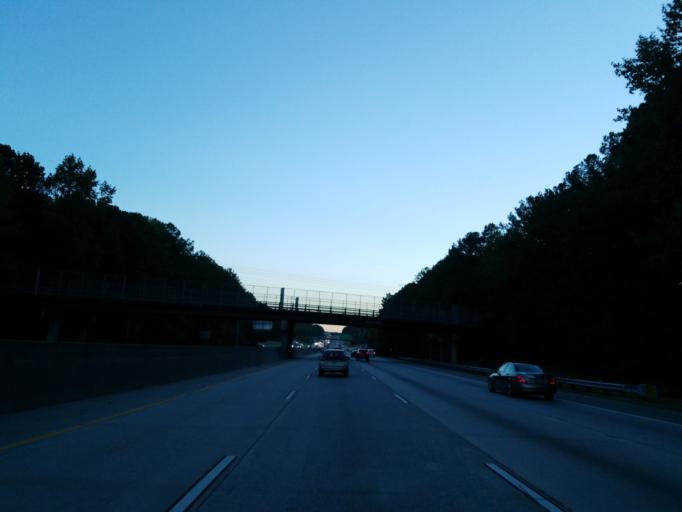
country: US
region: Georgia
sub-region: Fulton County
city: Alpharetta
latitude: 34.0755
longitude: -84.2685
